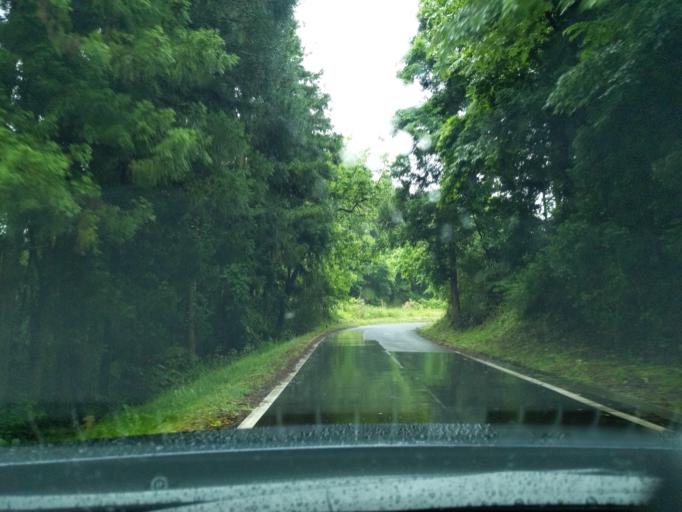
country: JP
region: Fukushima
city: Nihommatsu
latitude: 37.5809
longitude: 140.5420
